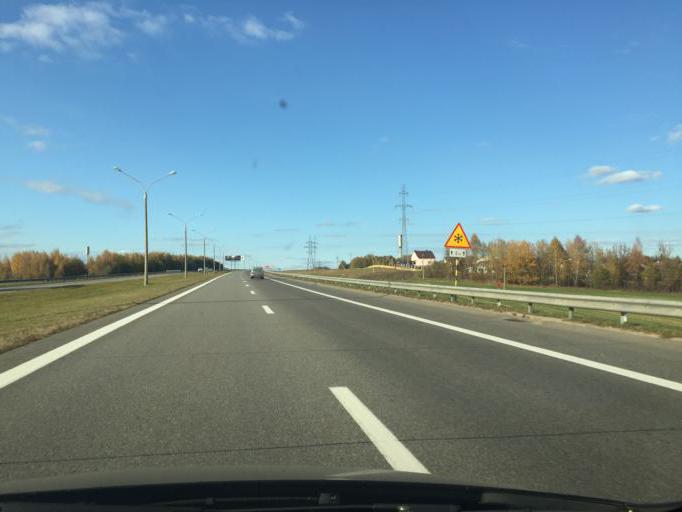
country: BY
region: Minsk
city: Slabada
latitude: 53.9847
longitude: 27.9281
